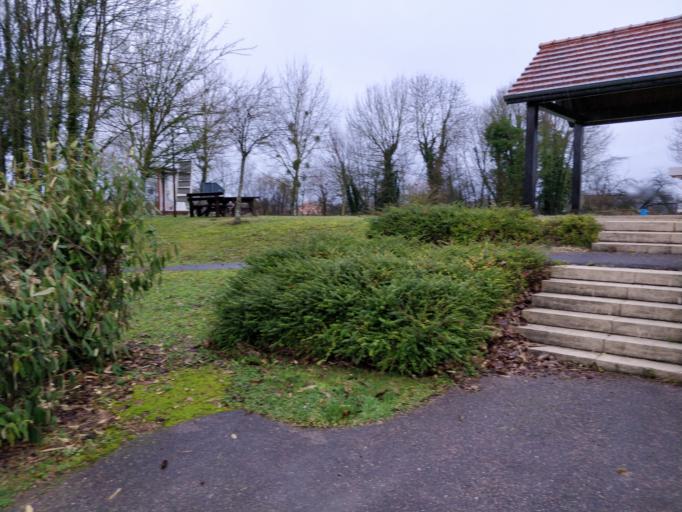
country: FR
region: Champagne-Ardenne
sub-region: Departement de la Marne
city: Frignicourt
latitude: 48.6660
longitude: 4.7337
